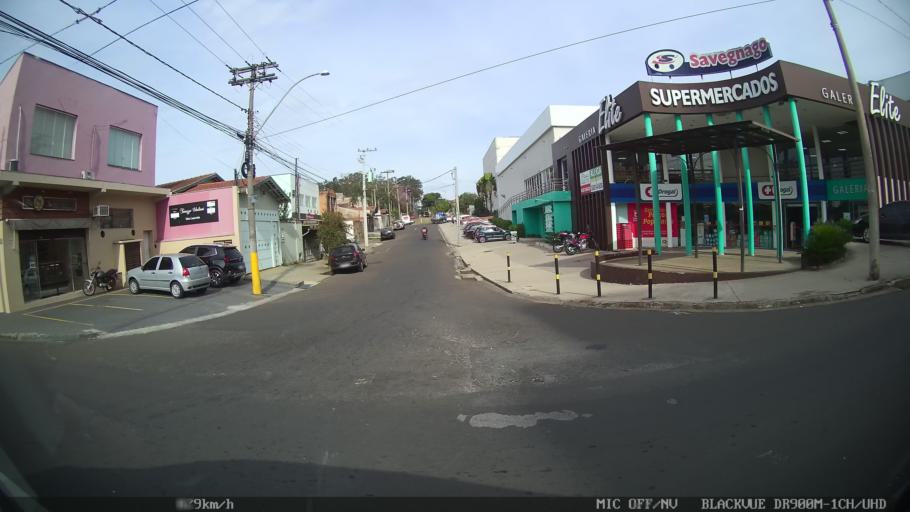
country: BR
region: Sao Paulo
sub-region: Piracicaba
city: Piracicaba
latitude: -22.7466
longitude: -47.6345
